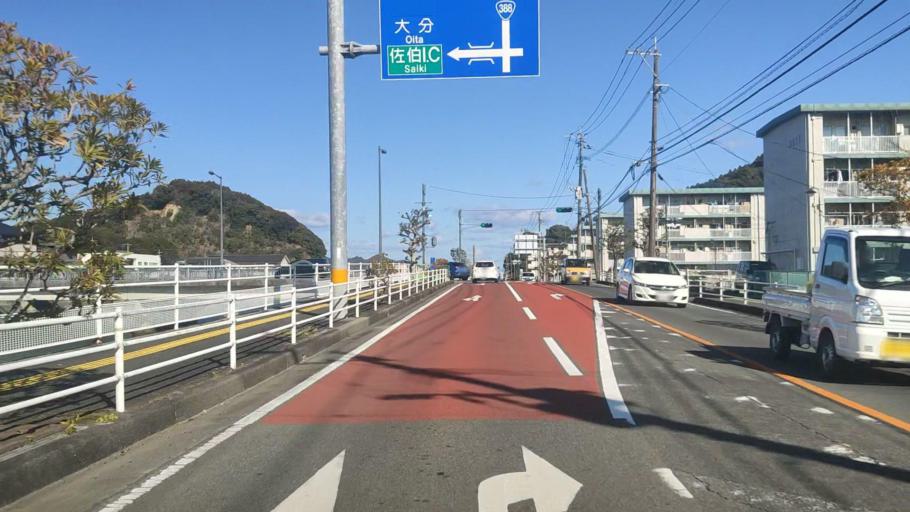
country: JP
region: Oita
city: Saiki
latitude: 32.9552
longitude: 131.9087
